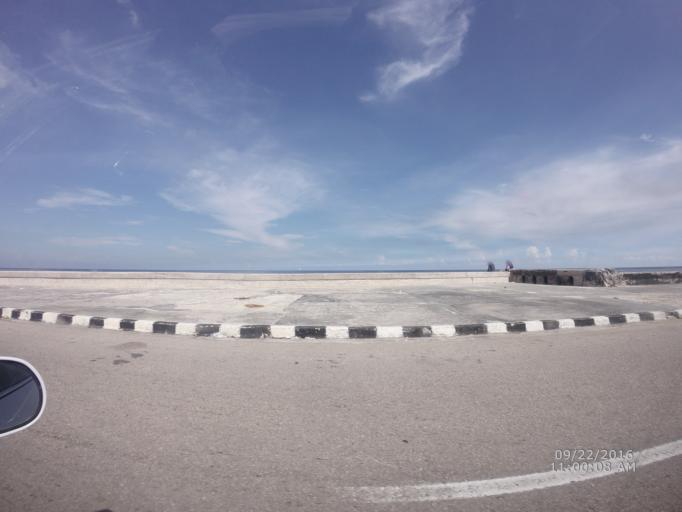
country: CU
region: La Habana
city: Havana
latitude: 23.1453
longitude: -82.3960
